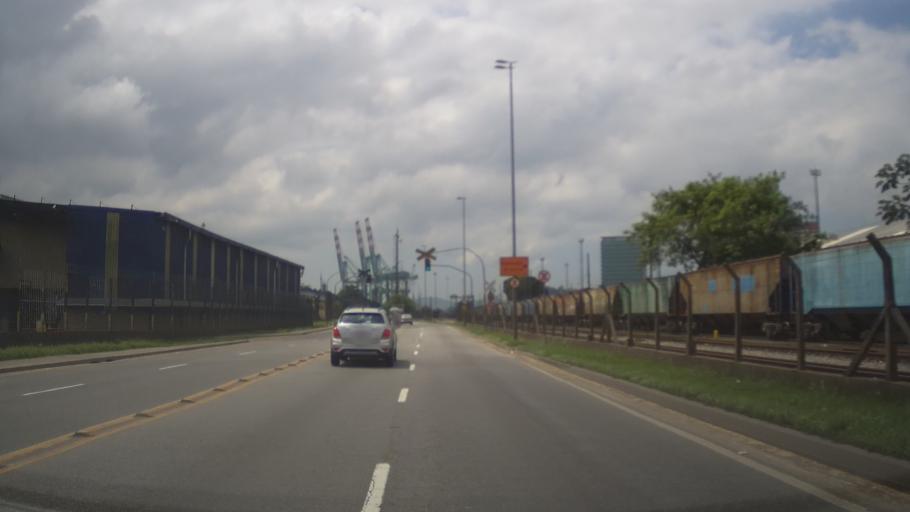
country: BR
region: Sao Paulo
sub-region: Santos
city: Santos
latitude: -23.9275
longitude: -46.3430
